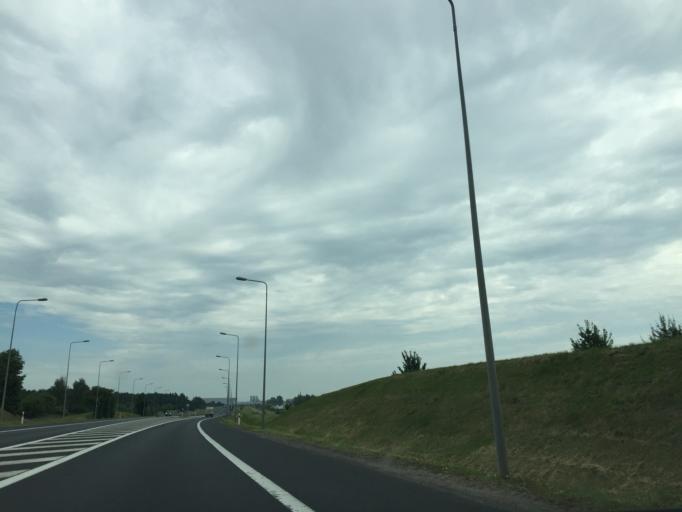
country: PL
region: Warmian-Masurian Voivodeship
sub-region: Powiat olsztynski
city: Biskupiec
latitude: 53.8454
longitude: 20.9466
